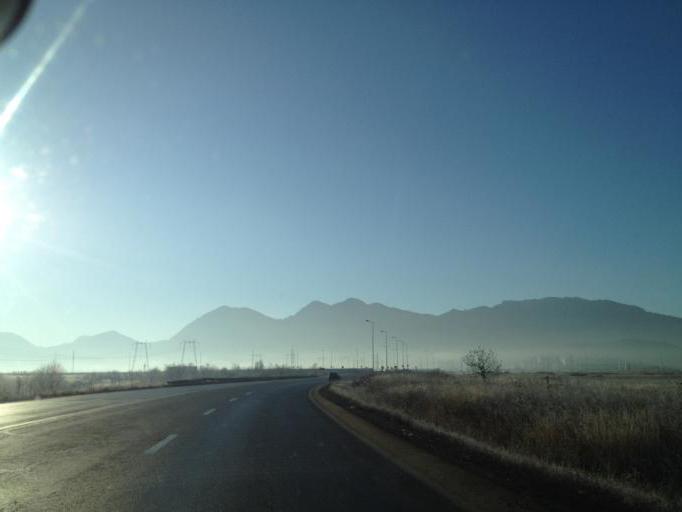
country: RO
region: Brasov
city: Brasov
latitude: 45.6405
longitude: 25.6565
